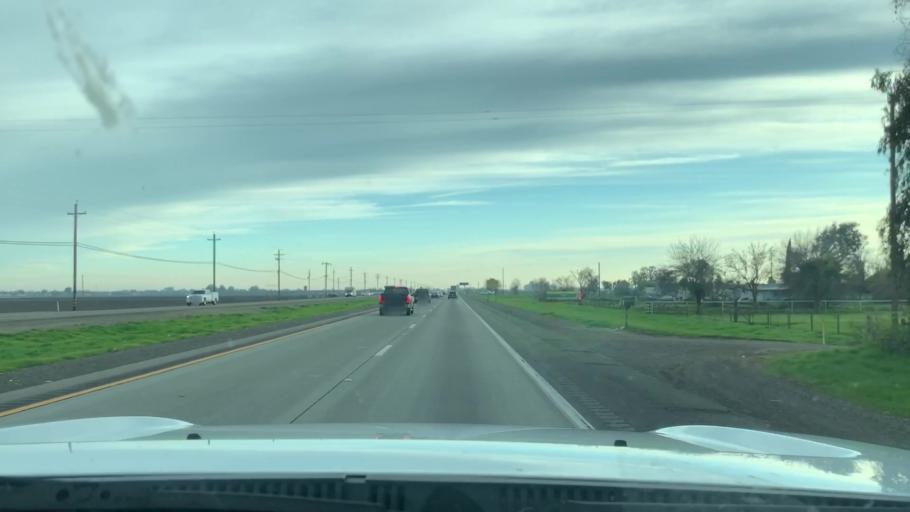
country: US
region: California
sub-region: Kings County
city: Lemoore
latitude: 36.3308
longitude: -119.8082
